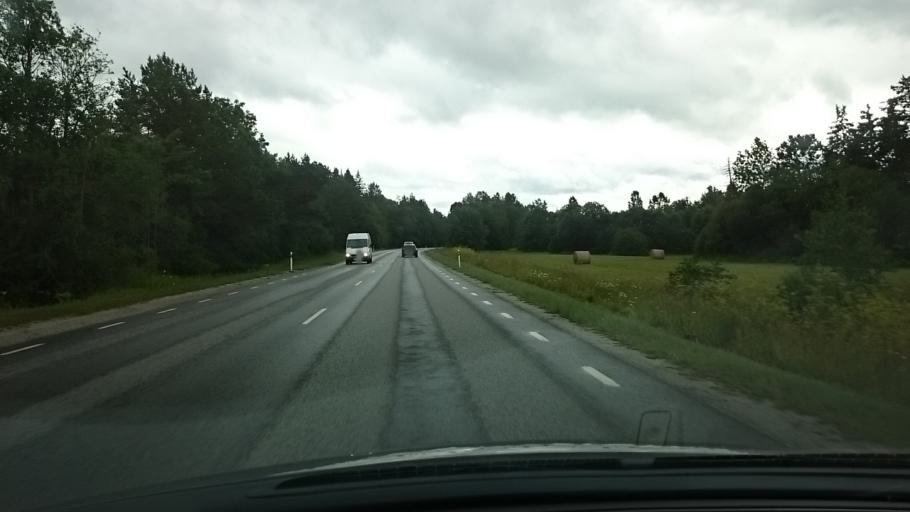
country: EE
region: Harju
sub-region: Keila linn
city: Keila
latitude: 59.2643
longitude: 24.2916
